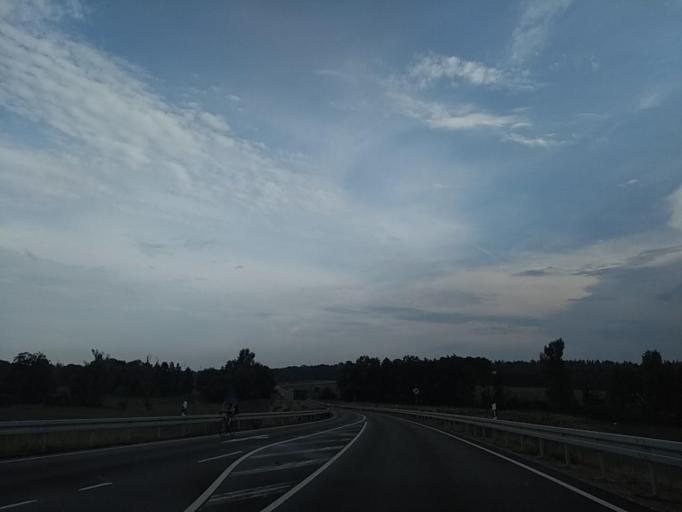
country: DE
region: Saxony-Anhalt
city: Muschwitz
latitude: 51.1915
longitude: 12.1255
